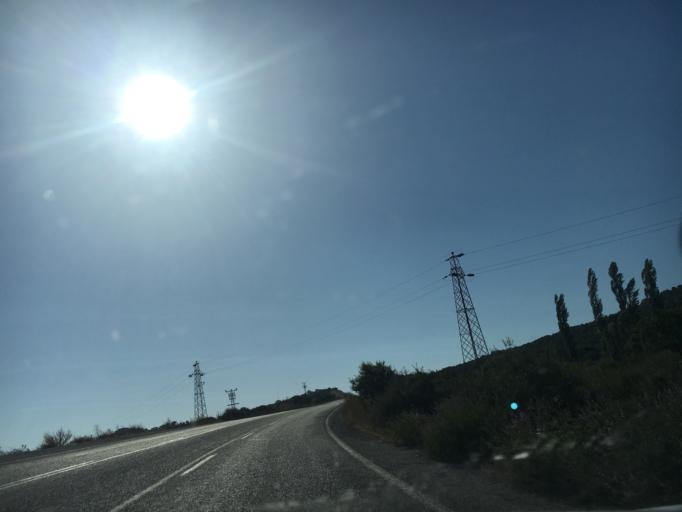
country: TR
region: Canakkale
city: Behram
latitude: 39.5047
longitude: 26.4002
